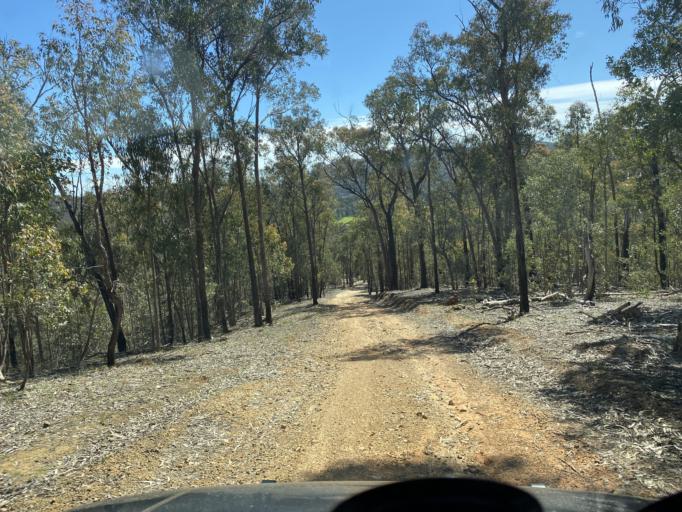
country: AU
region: Victoria
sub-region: Benalla
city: Benalla
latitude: -36.7178
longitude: 146.1809
